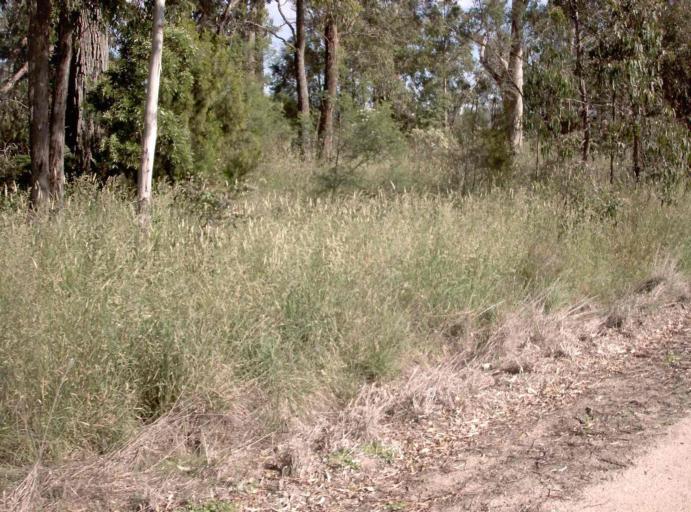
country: AU
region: Victoria
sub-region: East Gippsland
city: Lakes Entrance
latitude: -37.5307
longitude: 148.1537
